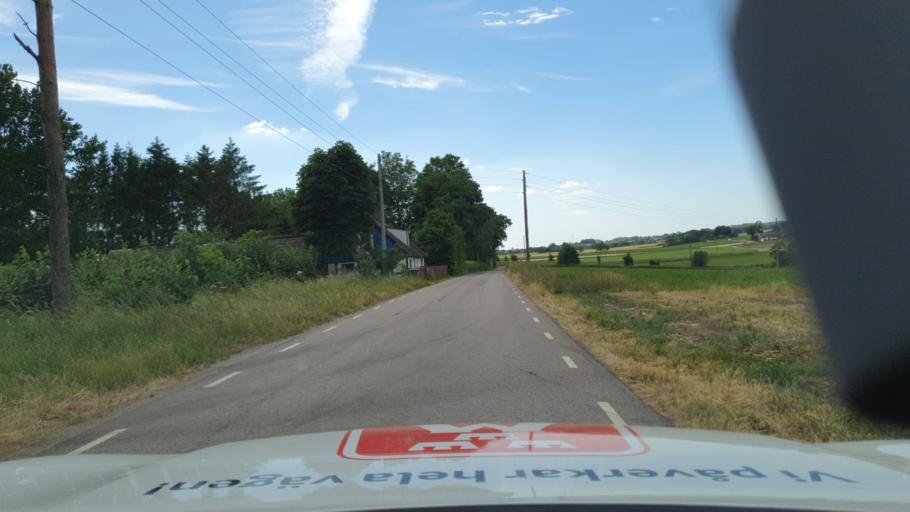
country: SE
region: Skane
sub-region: Sjobo Kommun
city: Sjoebo
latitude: 55.6341
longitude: 13.8134
